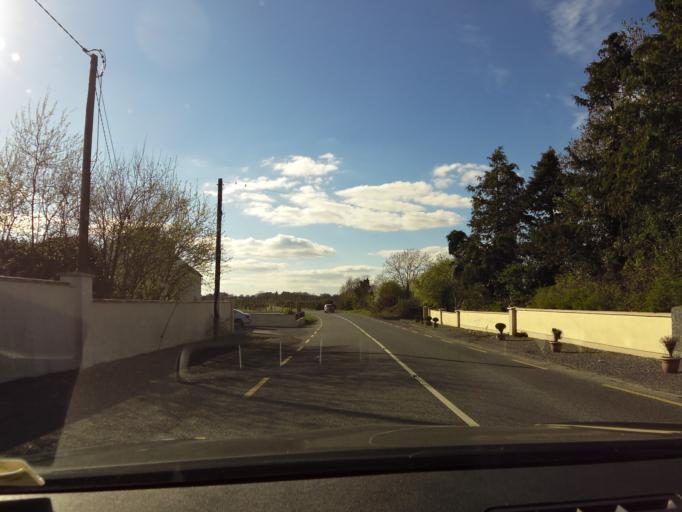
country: IE
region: Leinster
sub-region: Uibh Fhaili
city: Banagher
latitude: 53.1054
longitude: -8.0259
